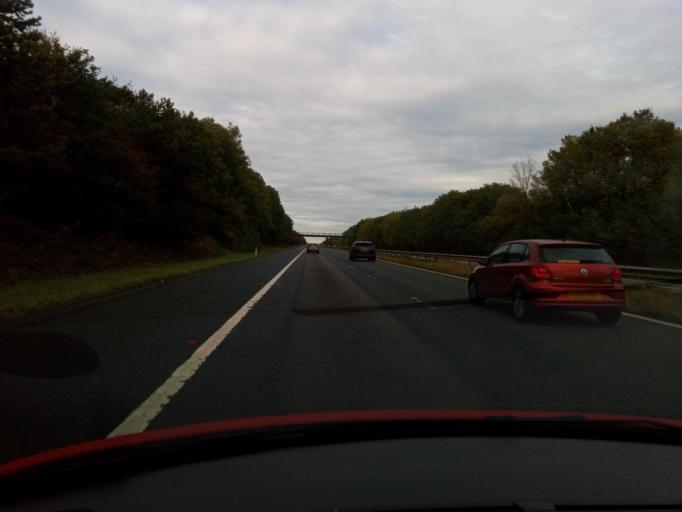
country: GB
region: England
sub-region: Darlington
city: High Coniscliffe
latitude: 54.5315
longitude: -1.6140
